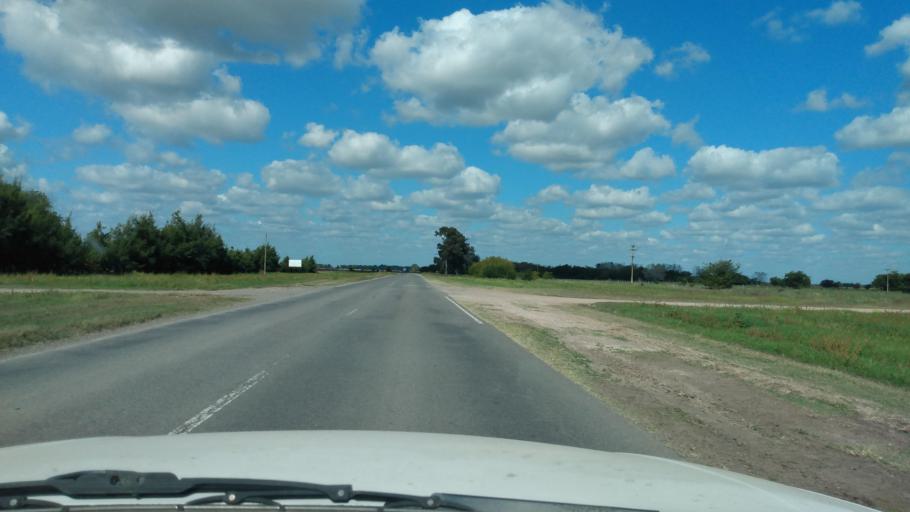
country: AR
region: Buenos Aires
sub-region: Partido de Navarro
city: Navarro
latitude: -34.9557
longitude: -59.3192
